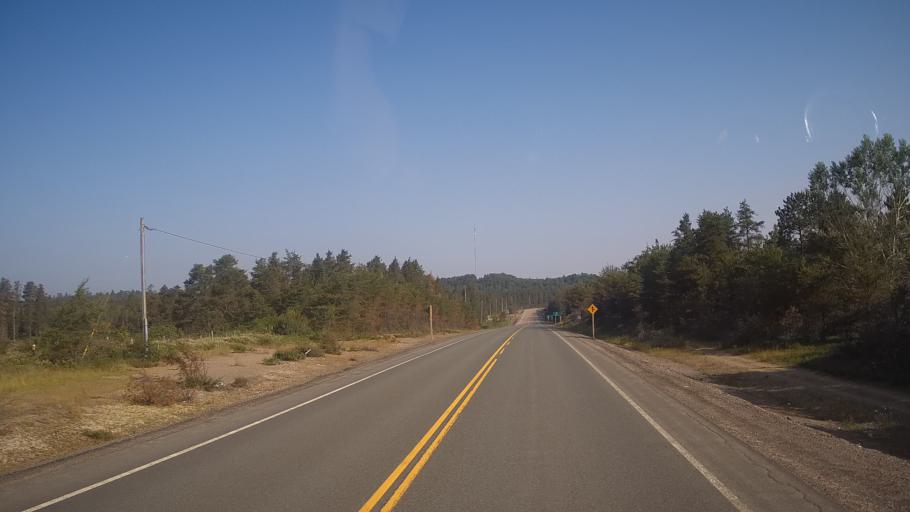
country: CA
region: Ontario
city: Rayside-Balfour
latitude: 46.7019
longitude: -81.5569
